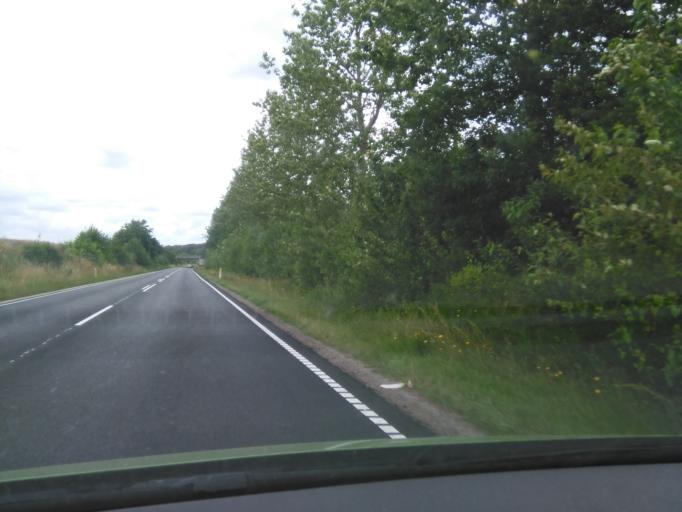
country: DK
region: Central Jutland
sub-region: Arhus Kommune
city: Beder
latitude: 56.0567
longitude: 10.1941
